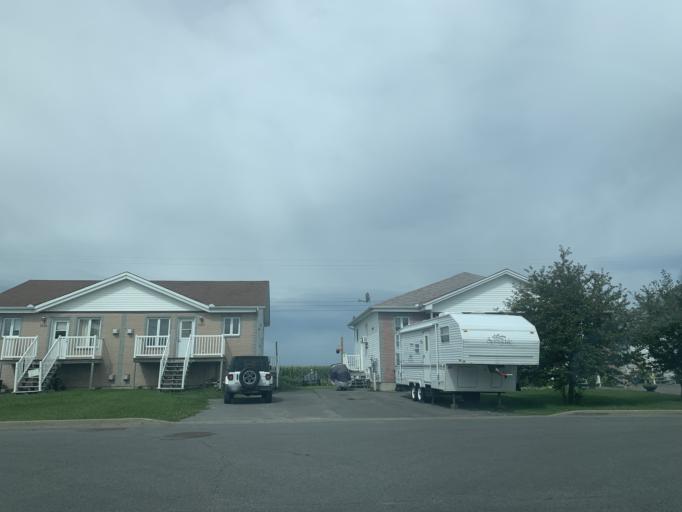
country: CA
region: Ontario
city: Hawkesbury
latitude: 45.6096
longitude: -74.6341
